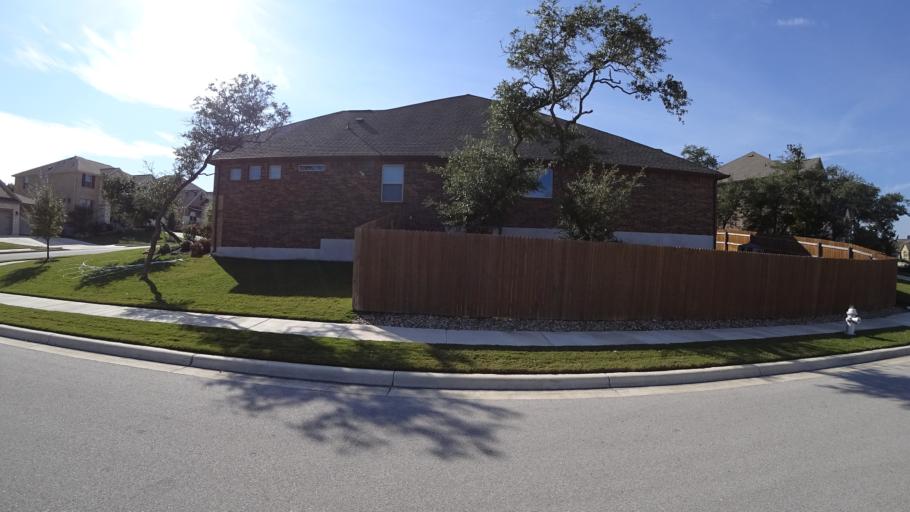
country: US
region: Texas
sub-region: Travis County
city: Barton Creek
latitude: 30.2302
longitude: -97.9083
